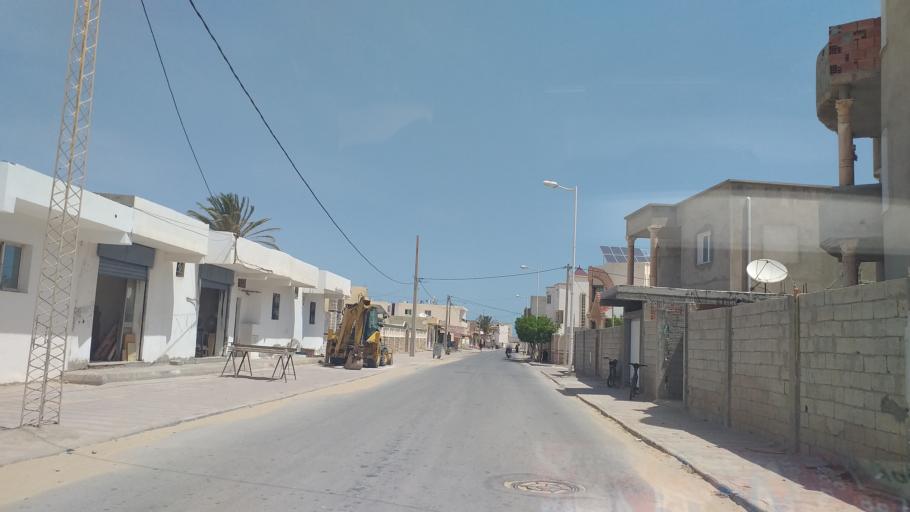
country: TN
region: Qabis
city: Gabes
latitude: 33.9472
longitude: 10.0686
